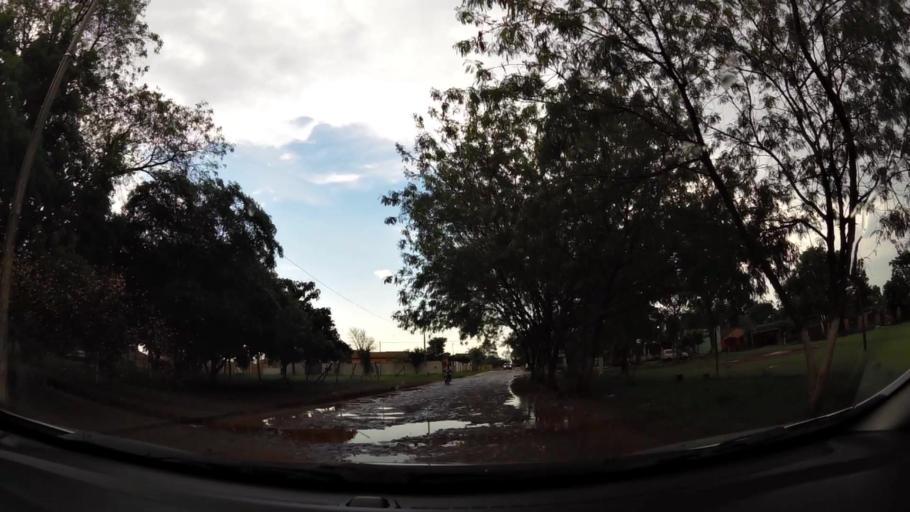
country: PY
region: Alto Parana
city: Presidente Franco
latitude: -25.5429
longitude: -54.6492
